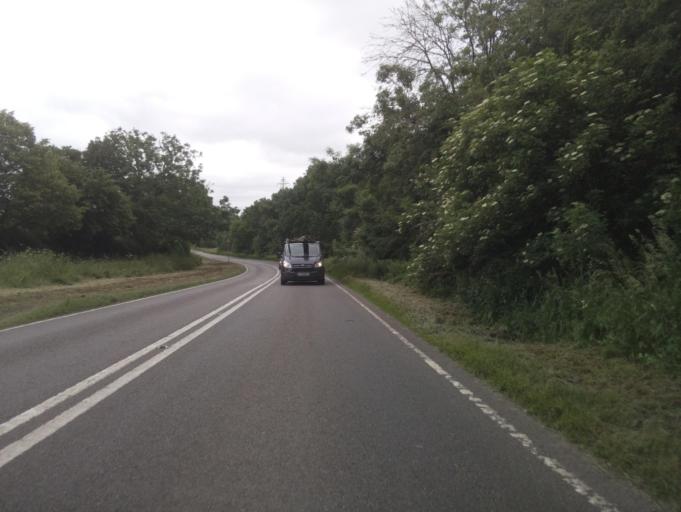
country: GB
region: England
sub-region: Leicestershire
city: Sileby
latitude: 52.8067
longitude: -1.0758
